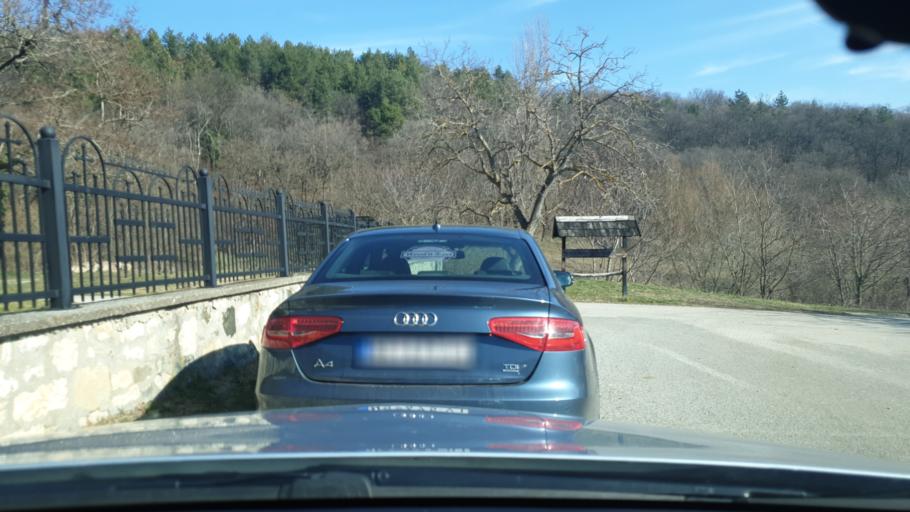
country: RS
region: Autonomna Pokrajina Vojvodina
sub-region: Sremski Okrug
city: Irig
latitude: 45.1279
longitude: 19.8468
